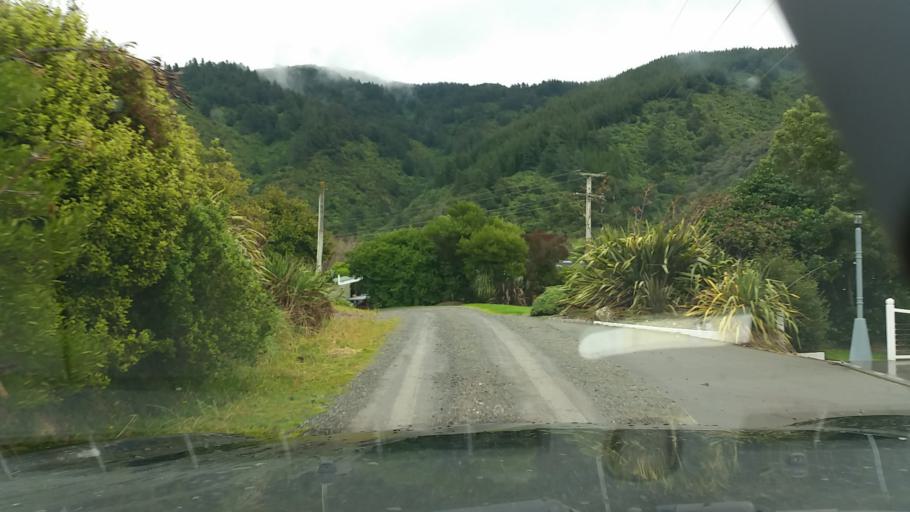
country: NZ
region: Marlborough
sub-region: Marlborough District
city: Picton
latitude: -41.2700
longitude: 174.0776
